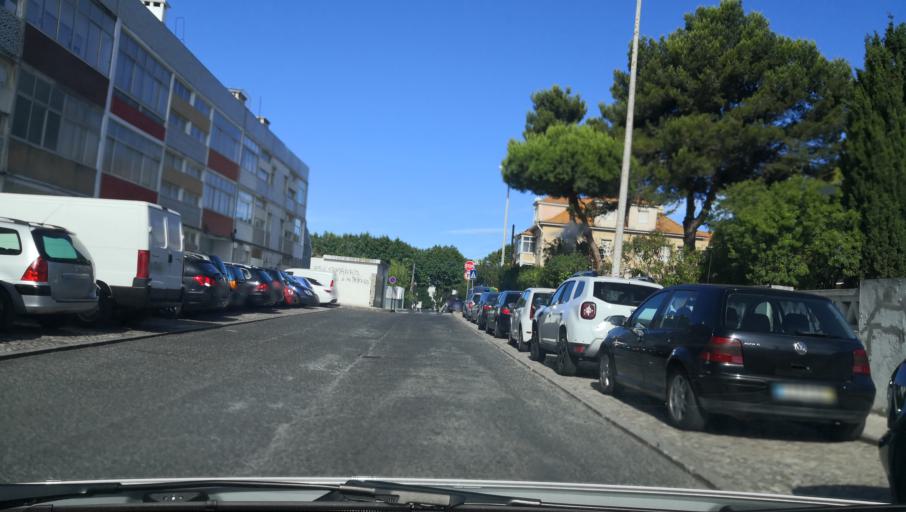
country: PT
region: Lisbon
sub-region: Cascais
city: Parede
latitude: 38.6883
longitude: -9.3385
